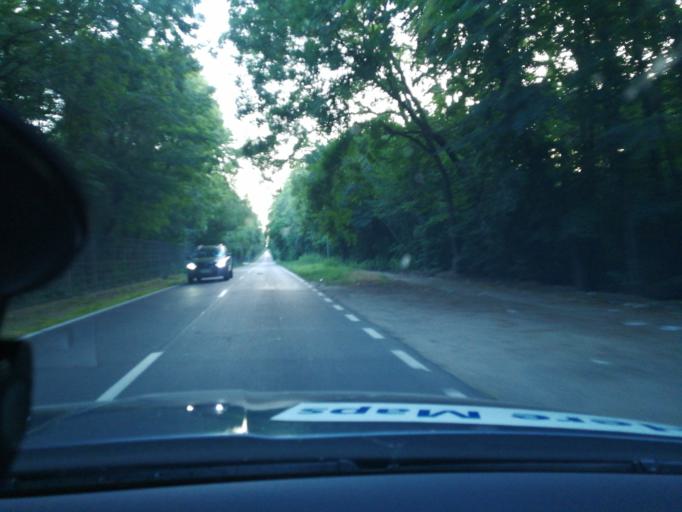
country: RO
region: Constanta
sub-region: Comuna Douazeci si Trei August
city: Douazeci si Trei August
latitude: 43.8750
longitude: 28.5960
